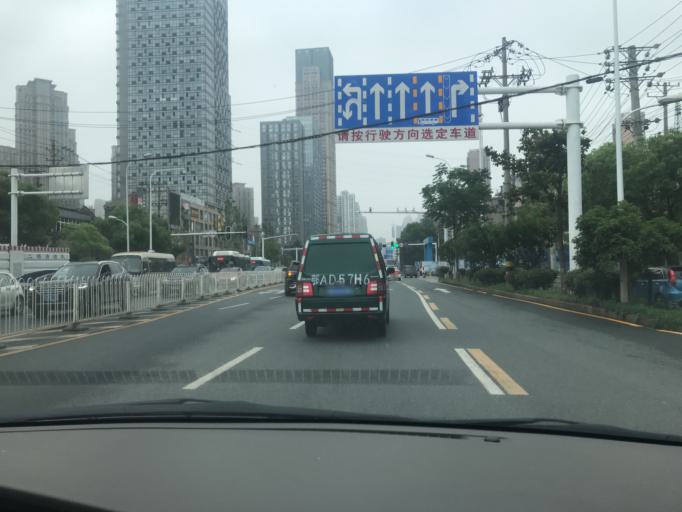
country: CN
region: Hubei
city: Jiang'an
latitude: 30.5802
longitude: 114.3168
